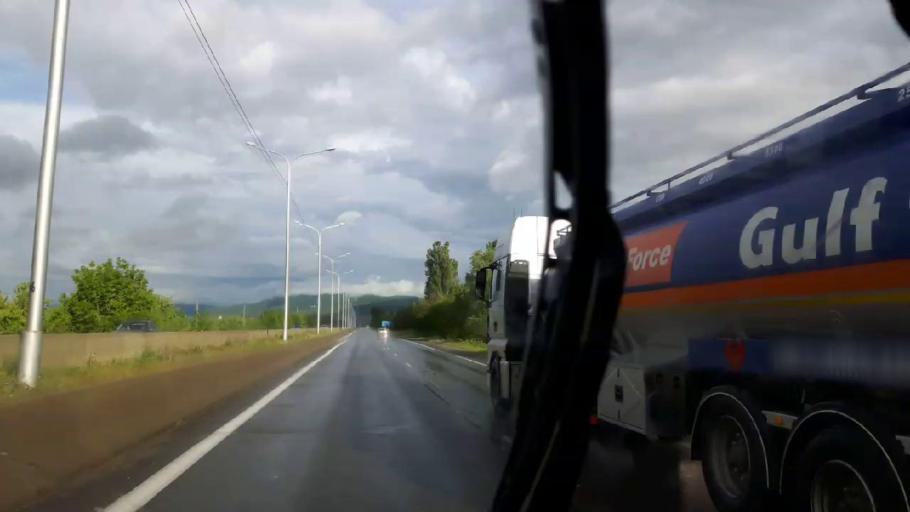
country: GE
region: Shida Kartli
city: Kaspi
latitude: 41.9215
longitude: 44.5465
